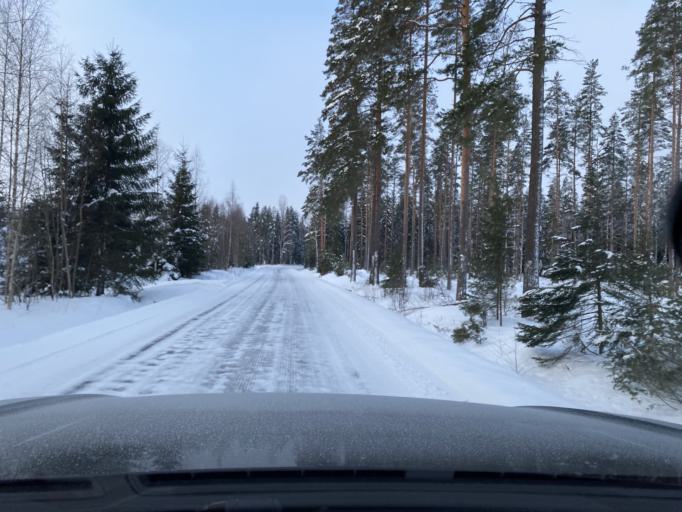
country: FI
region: Haeme
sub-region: Forssa
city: Tammela
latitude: 60.8625
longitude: 23.8718
